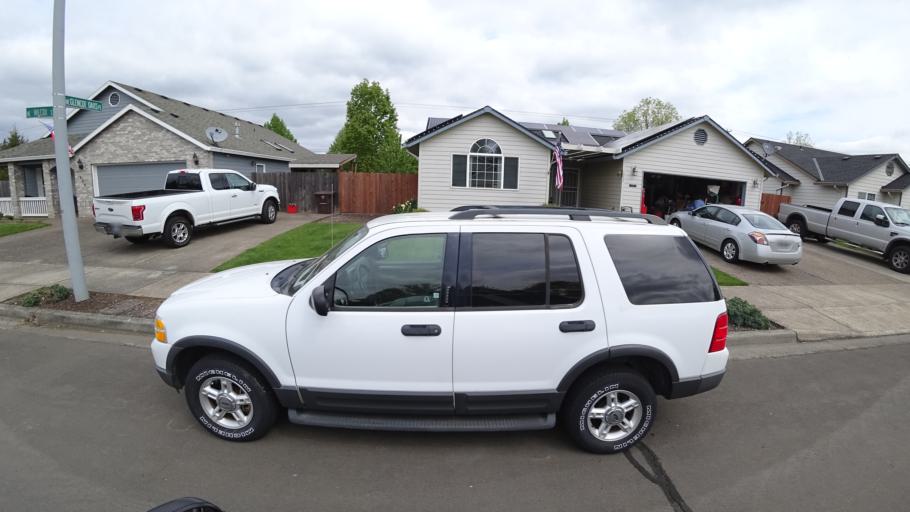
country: US
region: Oregon
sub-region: Washington County
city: Hillsboro
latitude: 45.5494
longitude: -122.9923
